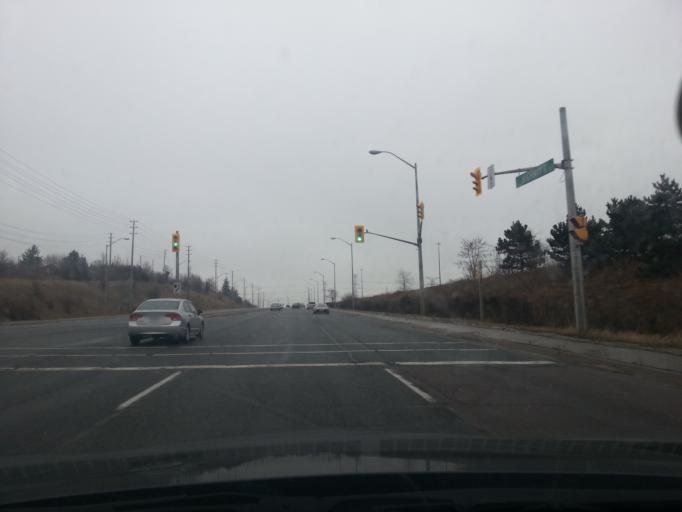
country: CA
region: Ontario
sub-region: York
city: Richmond Hill
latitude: 43.8317
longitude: -79.4400
